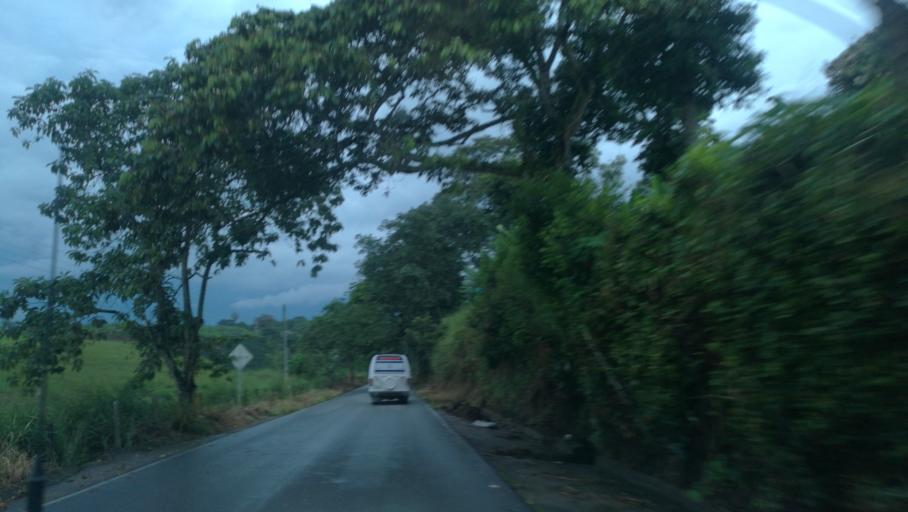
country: CO
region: Quindio
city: Montenegro
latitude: 4.5107
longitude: -75.7576
